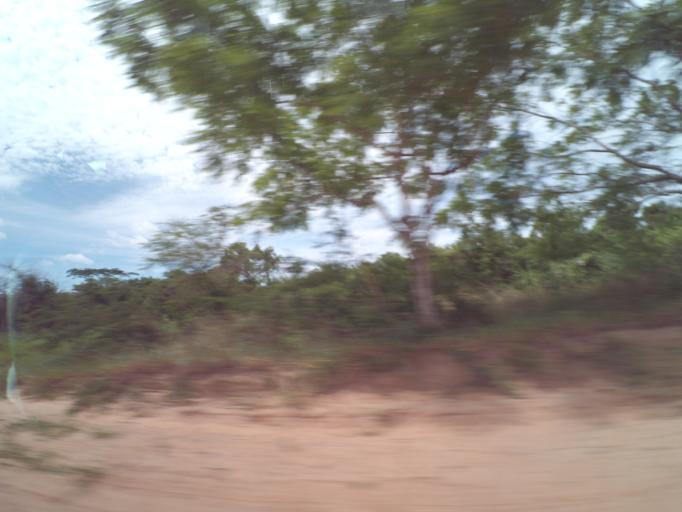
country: BO
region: Santa Cruz
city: Santa Cruz de la Sierra
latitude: -17.8977
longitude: -63.1765
